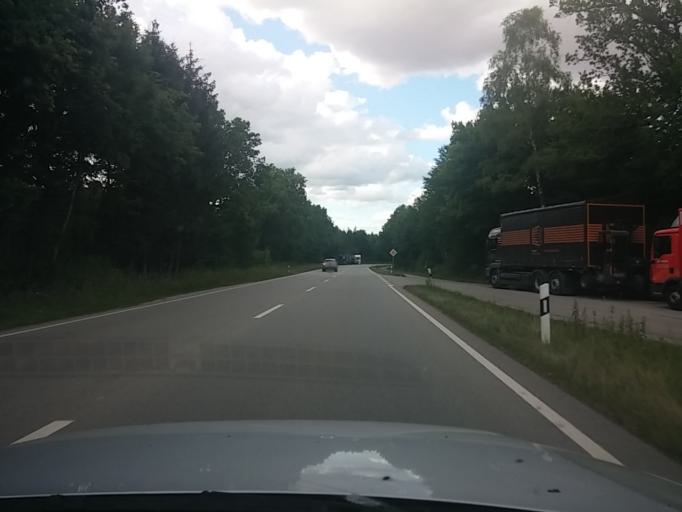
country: DE
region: Bavaria
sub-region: Upper Bavaria
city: Putzbrunn
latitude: 48.0893
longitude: 11.7214
